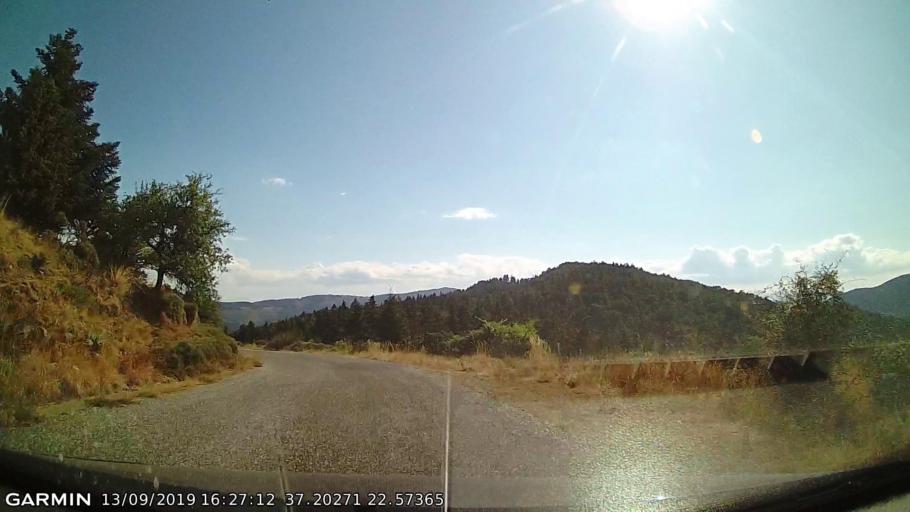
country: GR
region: Peloponnese
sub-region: Nomos Lakonias
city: Kariai
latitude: 37.2026
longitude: 22.5735
